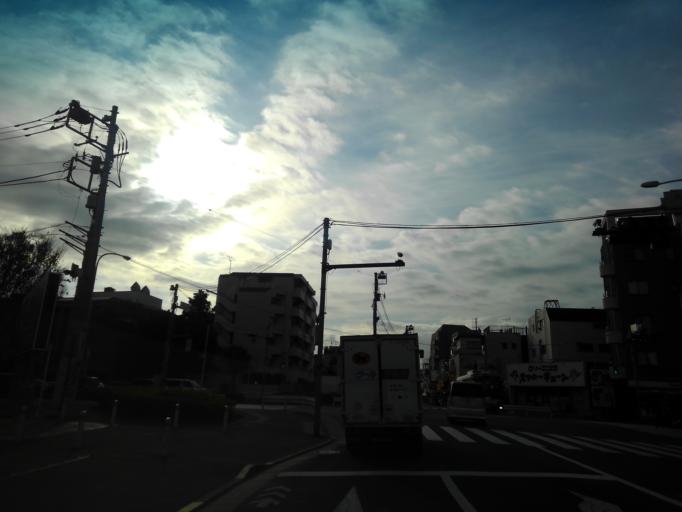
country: JP
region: Tokyo
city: Tokyo
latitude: 35.6688
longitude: 139.6728
